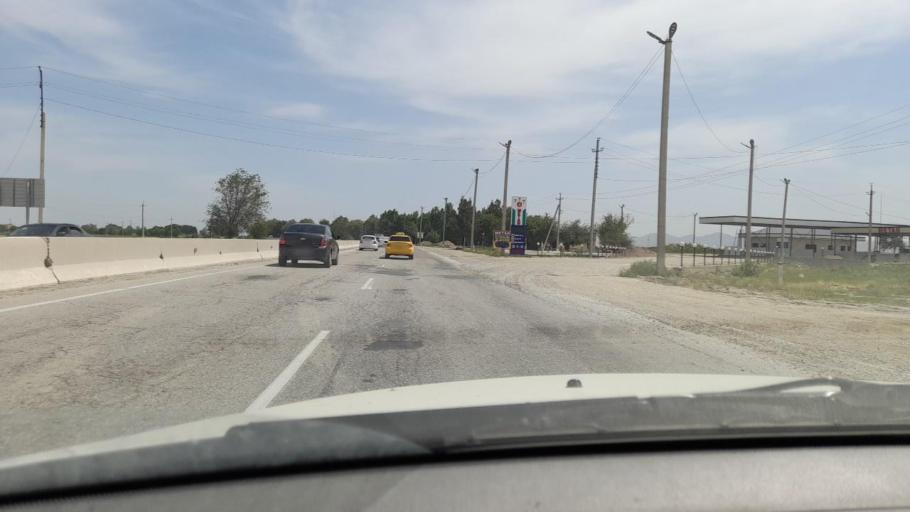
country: UZ
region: Navoiy
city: Karmana Shahri
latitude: 40.1291
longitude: 65.4134
